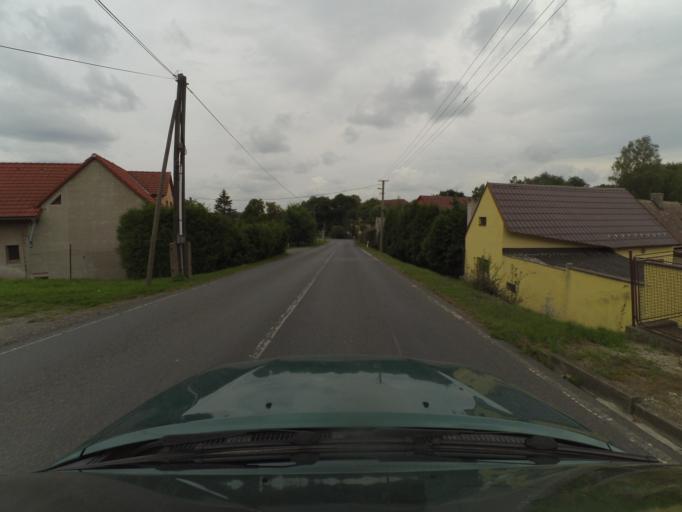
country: CZ
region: Plzensky
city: Kozlany
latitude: 50.0397
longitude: 13.6089
